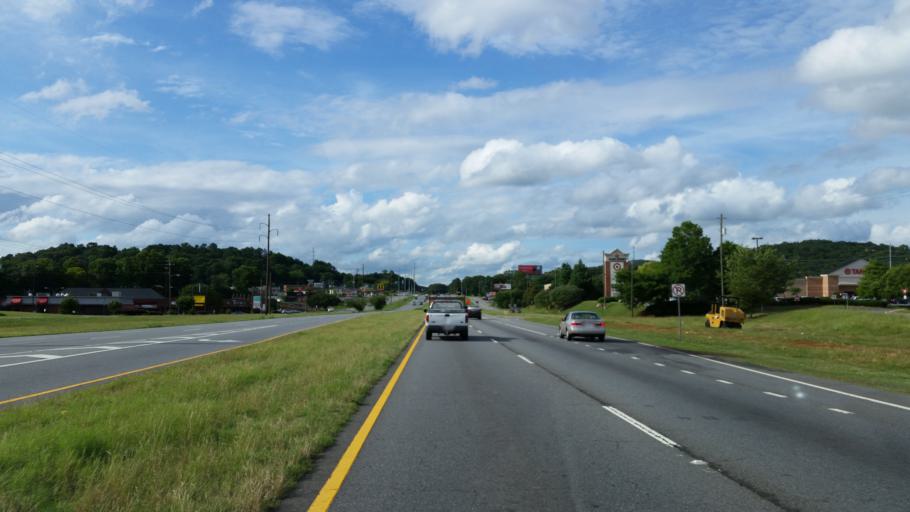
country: US
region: Georgia
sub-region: Bartow County
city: Cartersville
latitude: 34.1708
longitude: -84.7875
